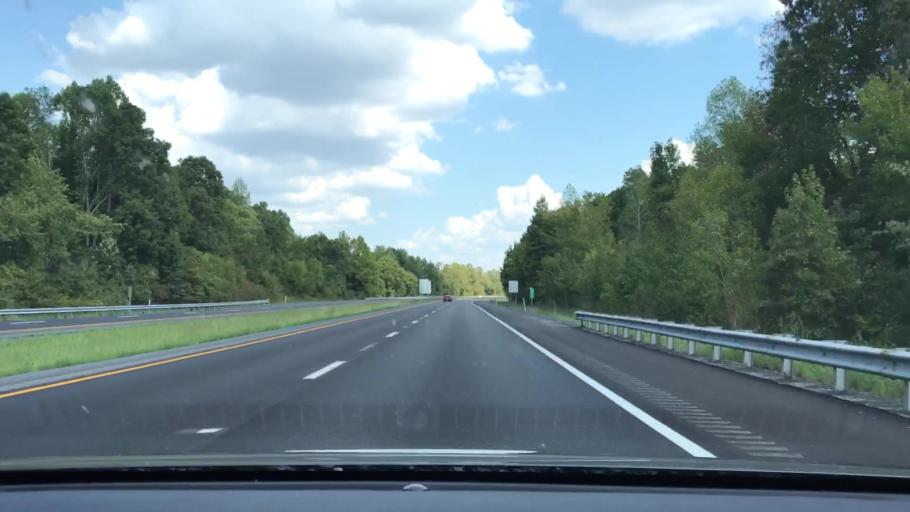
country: US
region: Kentucky
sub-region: Lyon County
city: Eddyville
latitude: 37.0807
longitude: -88.0730
